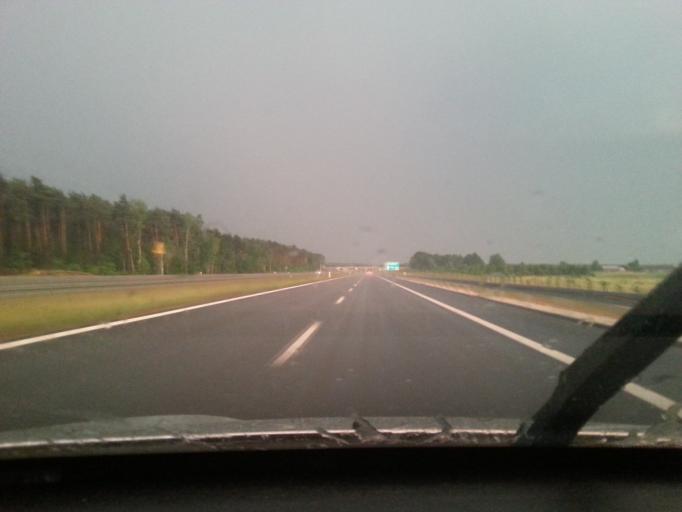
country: PL
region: Lodz Voivodeship
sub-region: Powiat pabianicki
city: Dobron
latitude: 51.6131
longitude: 19.2749
